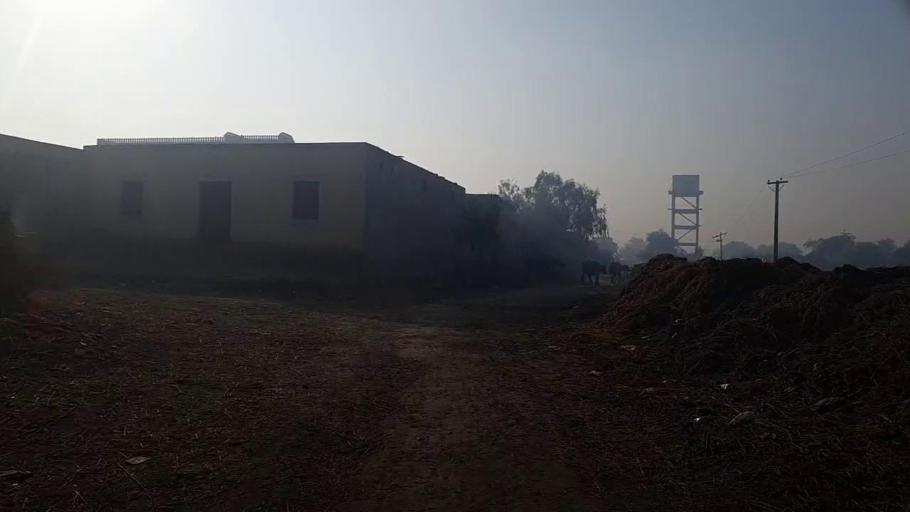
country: PK
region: Sindh
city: Mehar
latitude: 27.1359
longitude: 67.8232
